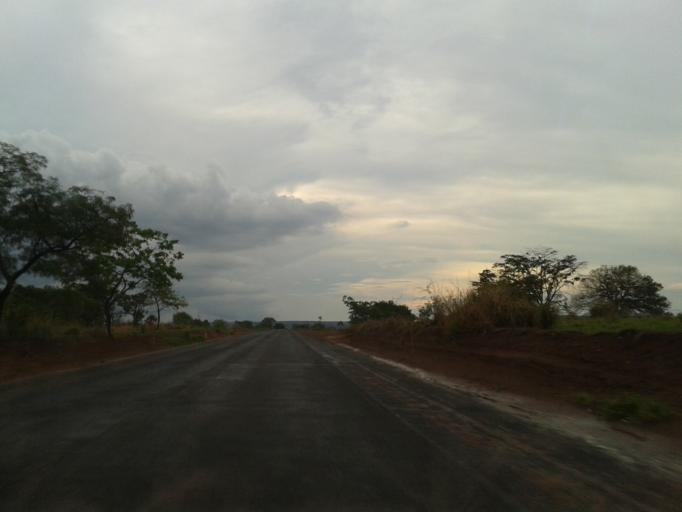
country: BR
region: Goias
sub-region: Quirinopolis
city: Quirinopolis
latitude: -18.1627
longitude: -50.4675
